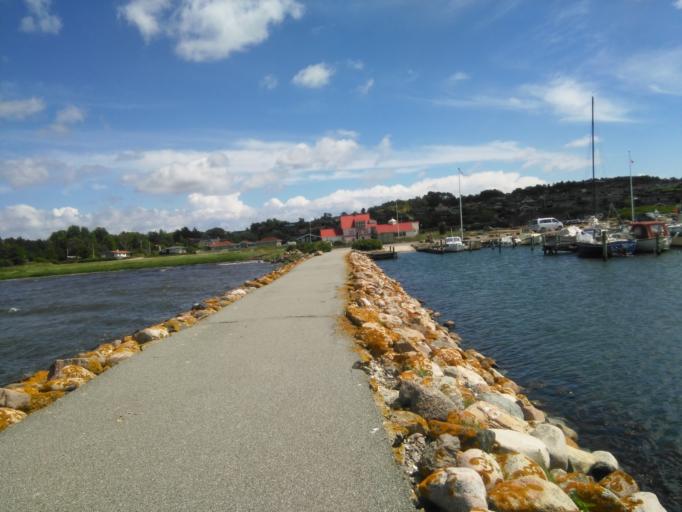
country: DK
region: Central Jutland
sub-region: Arhus Kommune
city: Logten
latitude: 56.1816
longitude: 10.3737
